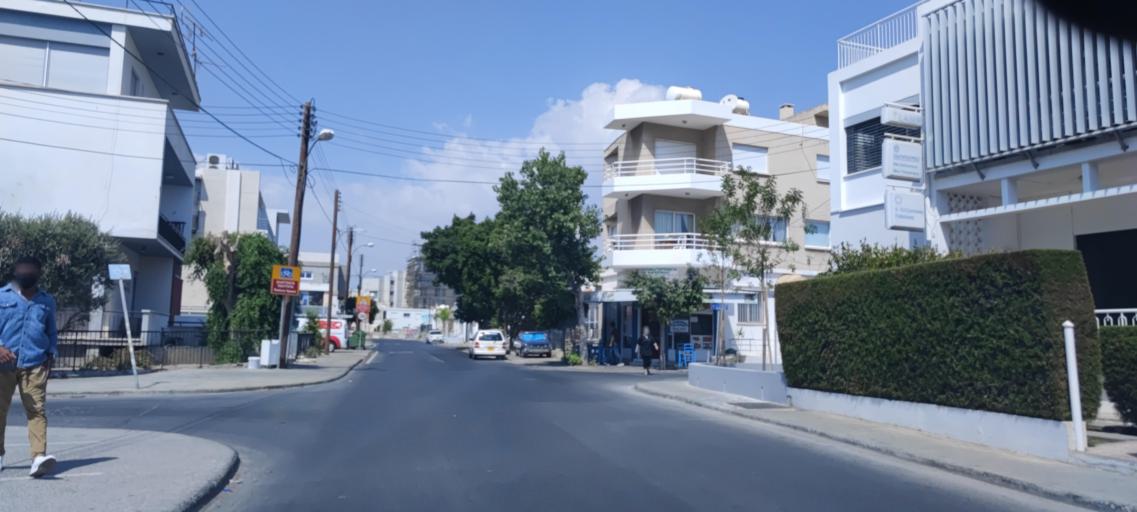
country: CY
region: Limassol
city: Limassol
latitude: 34.6817
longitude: 33.0350
